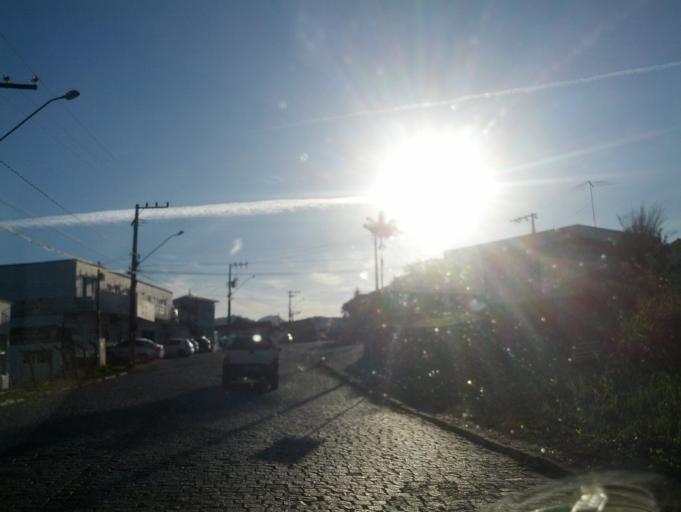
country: BR
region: Santa Catarina
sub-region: Indaial
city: Indaial
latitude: -26.8984
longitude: -49.2476
